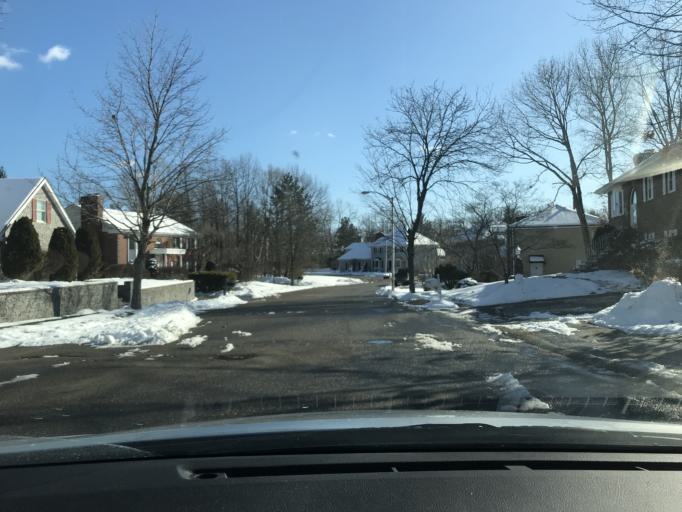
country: US
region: Massachusetts
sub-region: Essex County
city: Saugus
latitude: 42.4823
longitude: -71.0155
